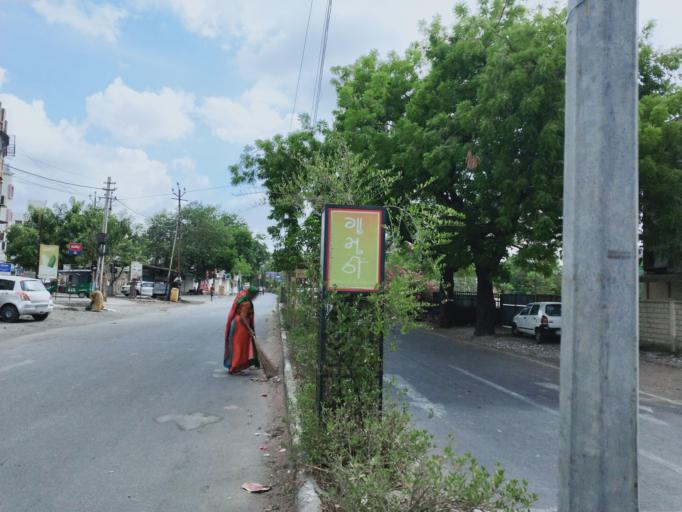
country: IN
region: Gujarat
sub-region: Bhavnagar
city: Bhavnagar
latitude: 21.7417
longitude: 72.1409
